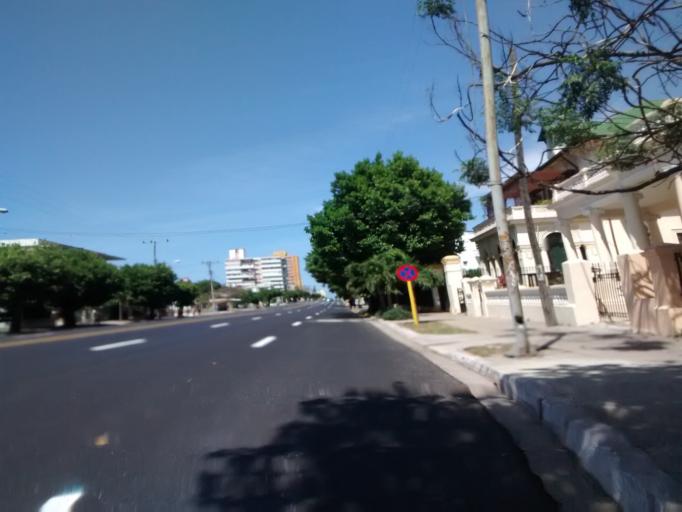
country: CU
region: La Habana
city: Havana
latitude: 23.1322
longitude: -82.3929
